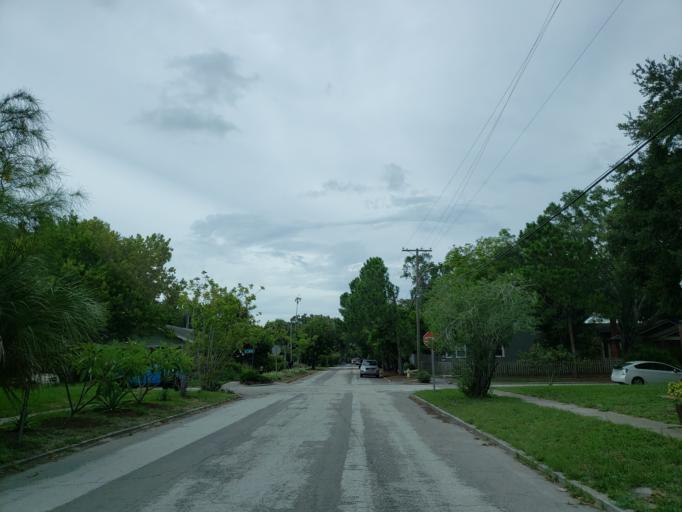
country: US
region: Florida
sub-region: Pinellas County
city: Saint Petersburg
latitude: 27.7779
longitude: -82.6769
